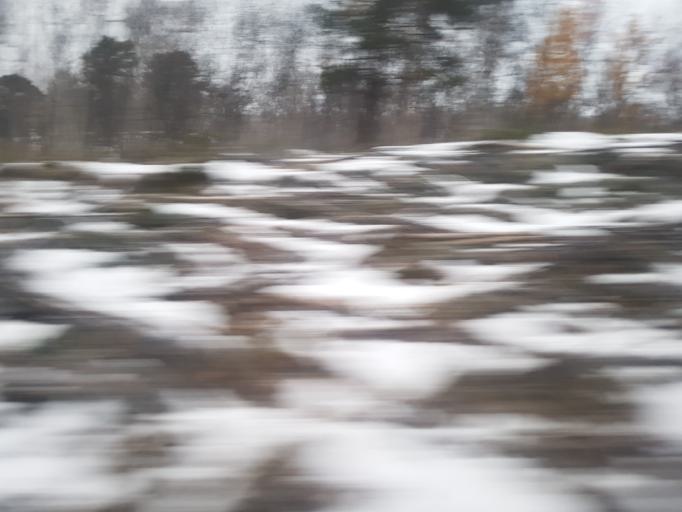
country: NO
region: Oppland
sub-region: Dovre
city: Dovre
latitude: 62.1781
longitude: 9.4543
